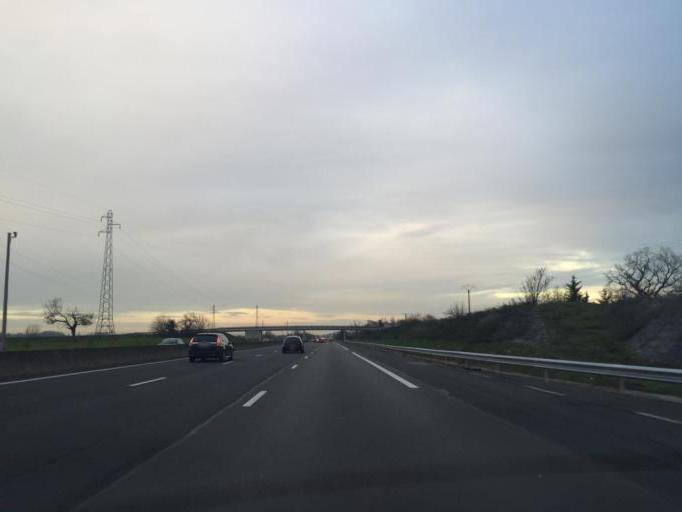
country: FR
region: Bourgogne
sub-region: Departement de Saone-et-Loire
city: La Chapelle-de-Guinchay
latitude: 46.2073
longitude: 4.7828
